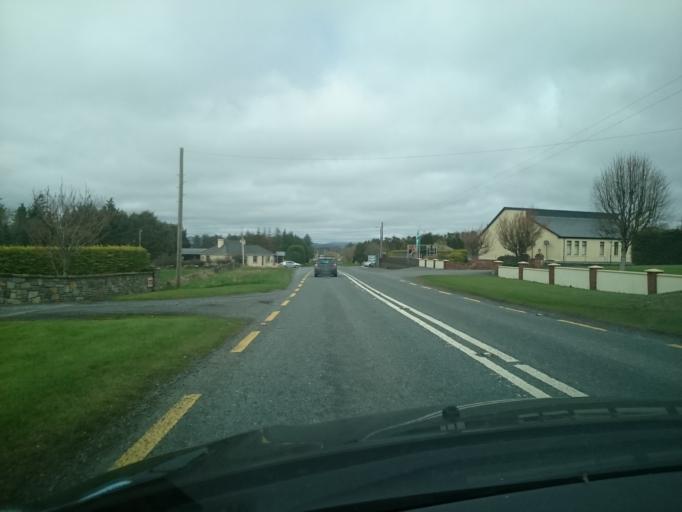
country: IE
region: Connaught
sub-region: Maigh Eo
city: Castlebar
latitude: 53.8321
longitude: -9.1838
